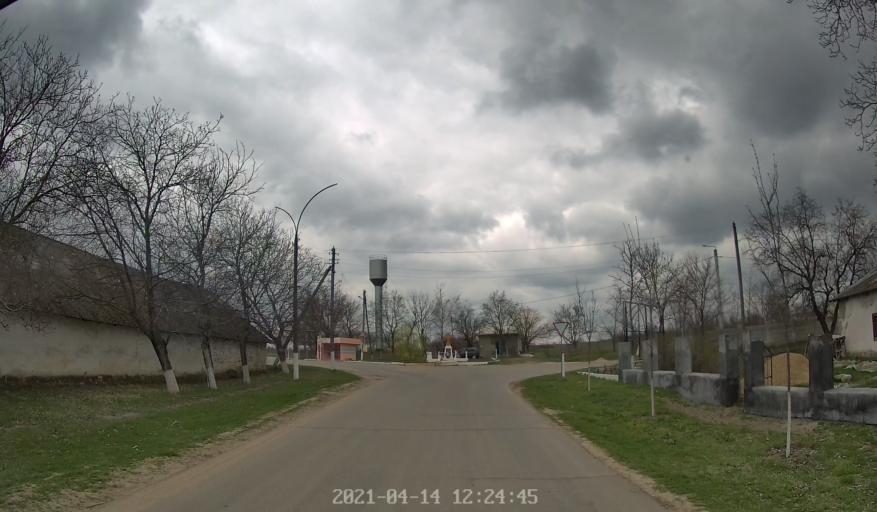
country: MD
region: Criuleni
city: Criuleni
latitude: 47.1717
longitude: 29.1932
